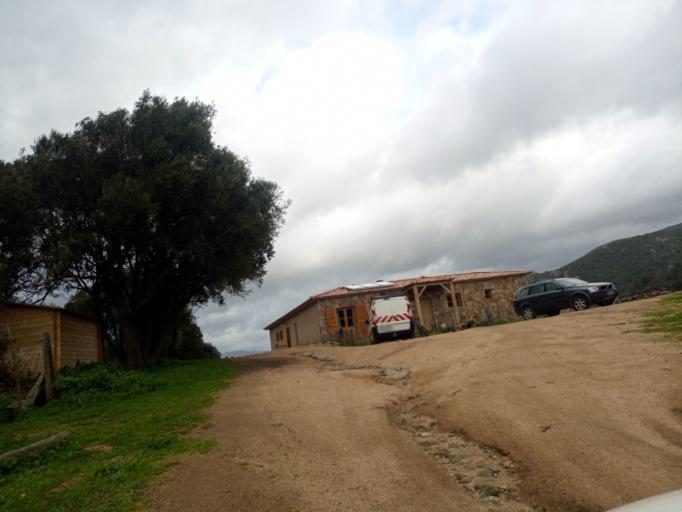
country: FR
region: Corsica
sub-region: Departement de la Corse-du-Sud
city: Sartene
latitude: 41.5238
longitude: 8.9510
